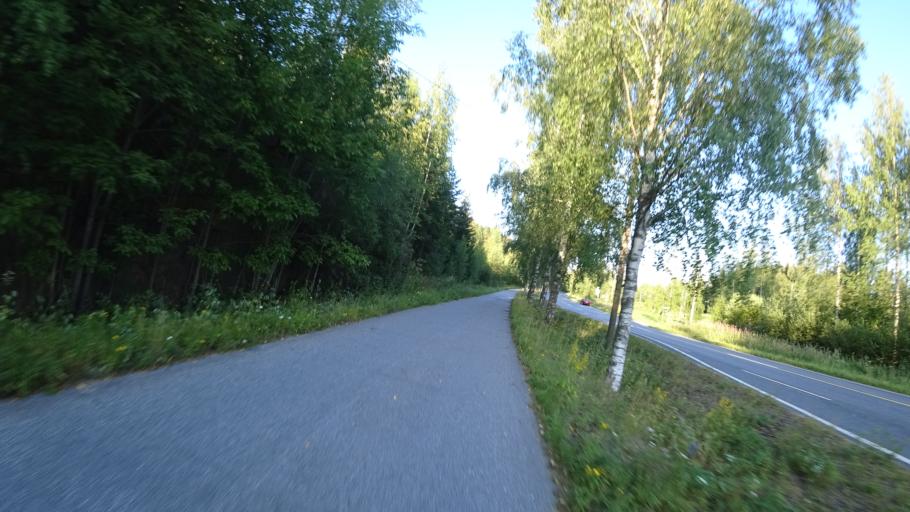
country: FI
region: Pirkanmaa
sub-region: Tampere
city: Nokia
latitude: 61.4666
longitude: 23.4227
